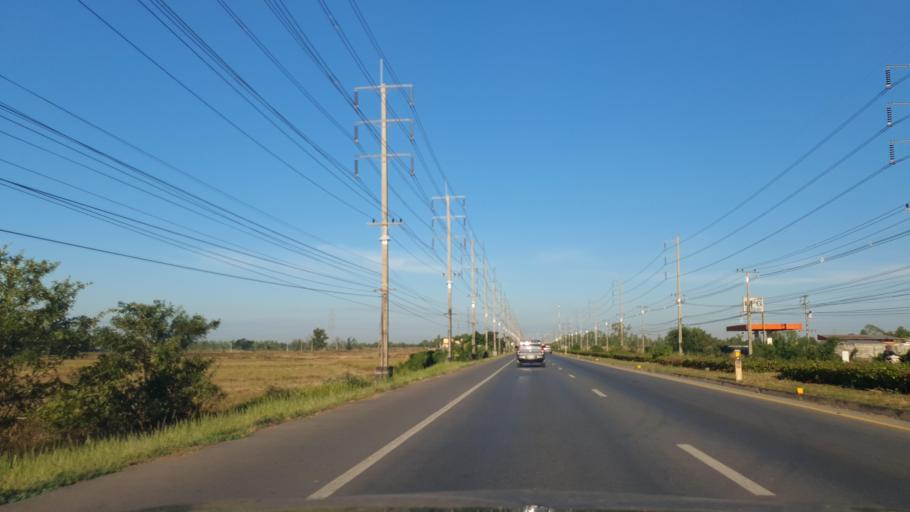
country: TH
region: Phitsanulok
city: Phrom Phiram
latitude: 16.9263
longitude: 100.1664
